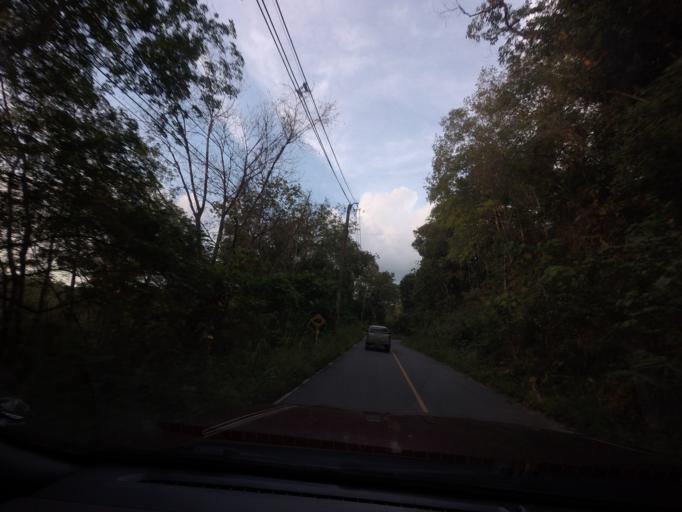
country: TH
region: Yala
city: Than To
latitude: 6.0076
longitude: 101.2204
